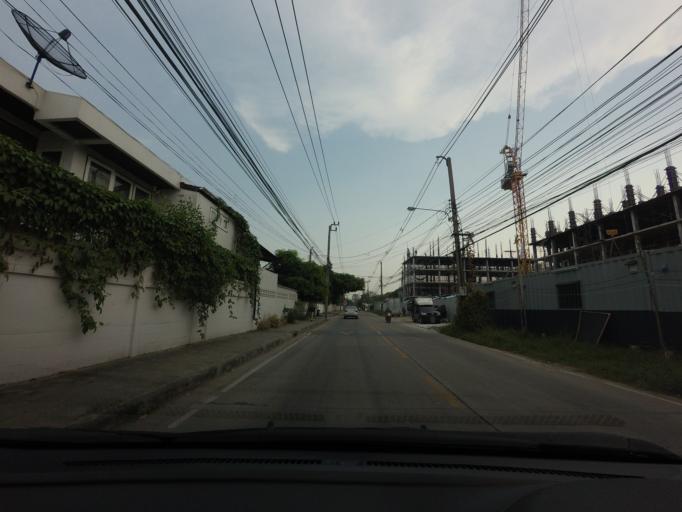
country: TH
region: Bangkok
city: Bang Kapi
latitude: 13.7523
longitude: 100.6265
